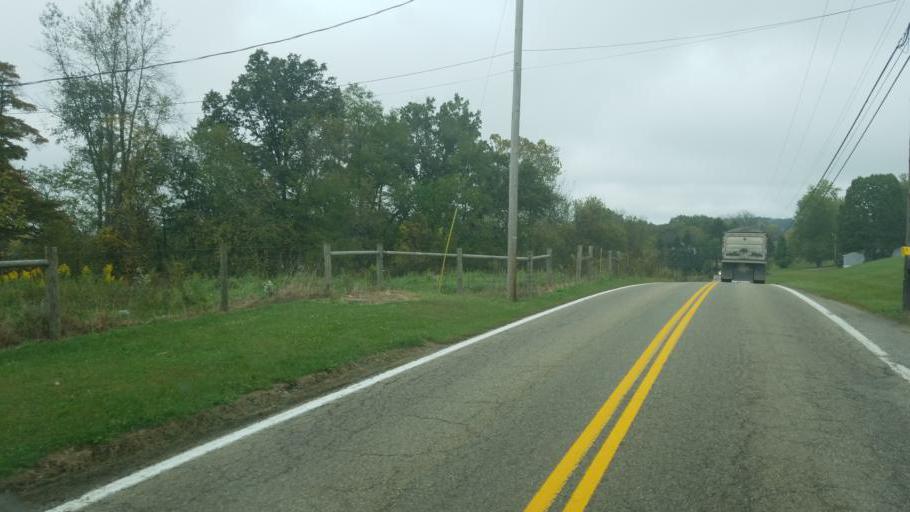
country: US
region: Ohio
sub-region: Stark County
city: Beach City
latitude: 40.6516
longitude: -81.5688
